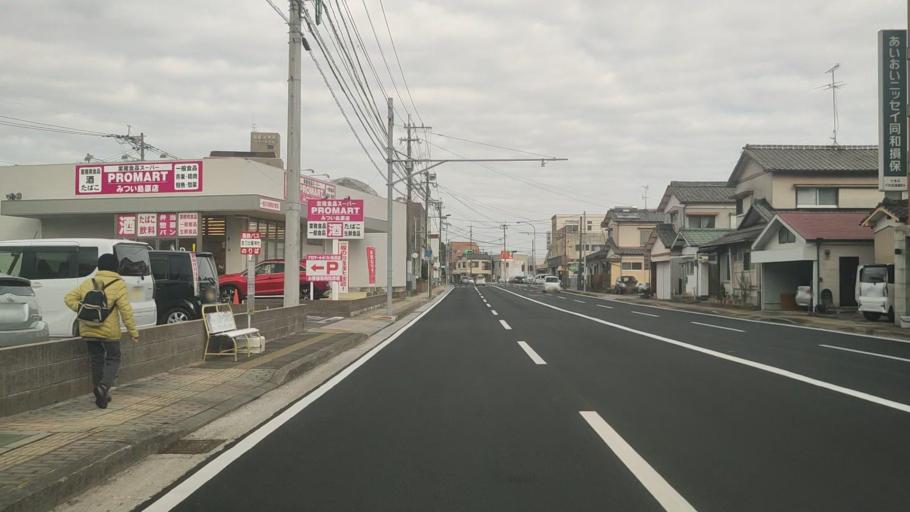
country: JP
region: Nagasaki
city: Shimabara
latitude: 32.7691
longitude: 130.3723
